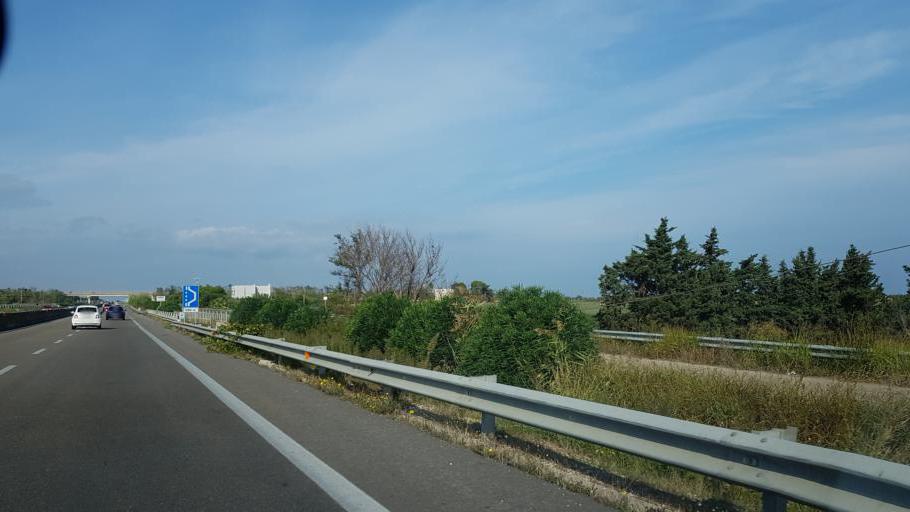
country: IT
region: Apulia
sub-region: Provincia di Brindisi
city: Brindisi
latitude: 40.6865
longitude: 17.8295
